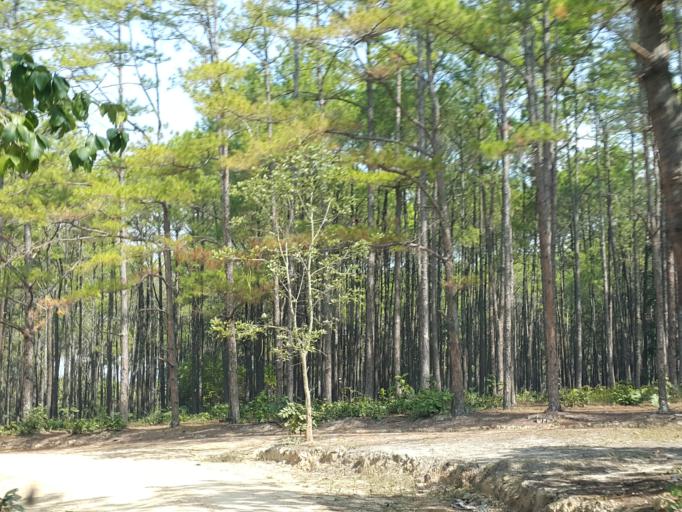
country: TH
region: Chiang Mai
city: Hot
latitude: 18.1421
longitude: 98.4308
